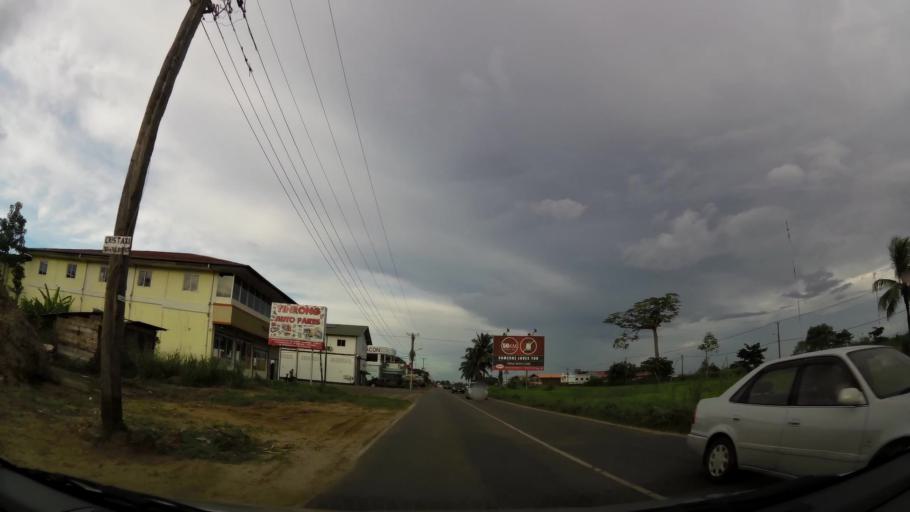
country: SR
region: Paramaribo
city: Paramaribo
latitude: 5.8564
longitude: -55.1608
